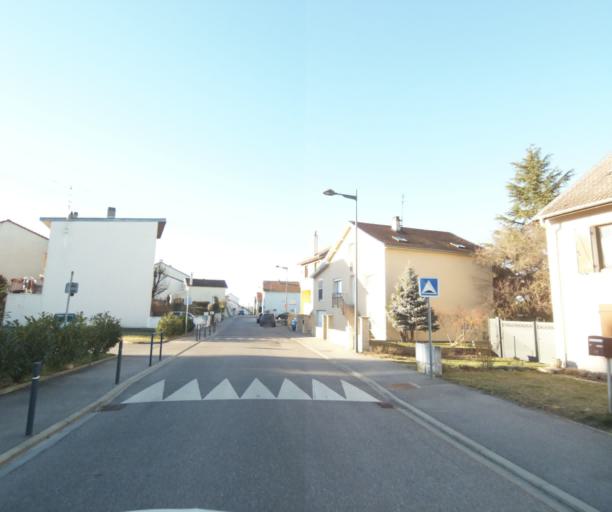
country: FR
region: Lorraine
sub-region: Departement de Meurthe-et-Moselle
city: Laneuveville-devant-Nancy
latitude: 48.6518
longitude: 6.2277
